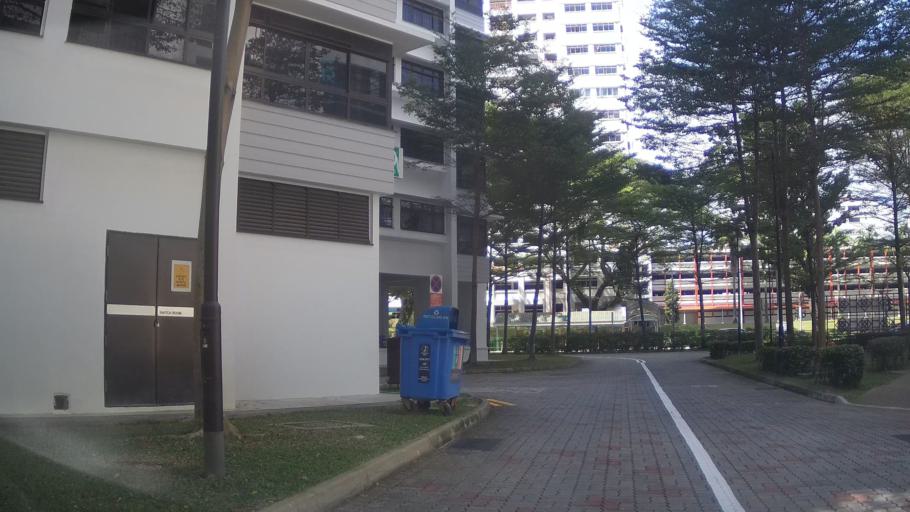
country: MY
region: Johor
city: Johor Bahru
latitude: 1.3380
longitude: 103.7218
